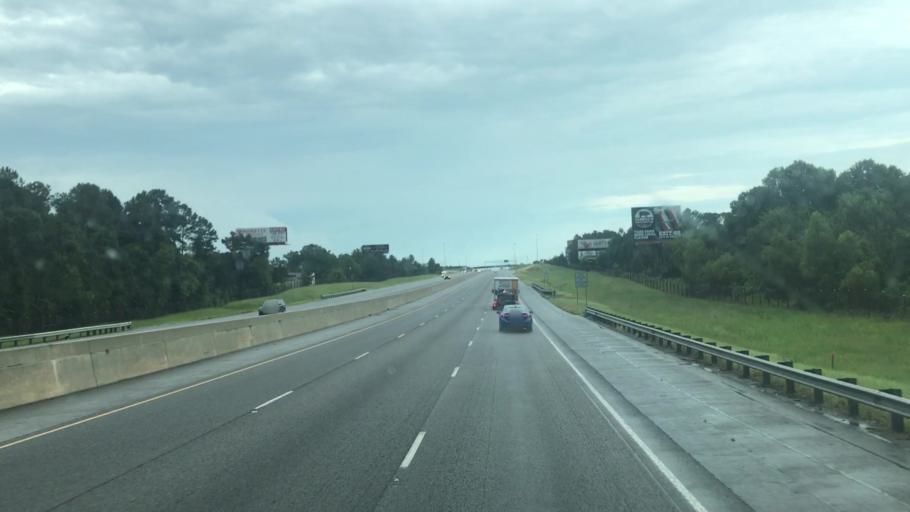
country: US
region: Georgia
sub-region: Crisp County
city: Cordele
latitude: 31.8447
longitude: -83.7165
